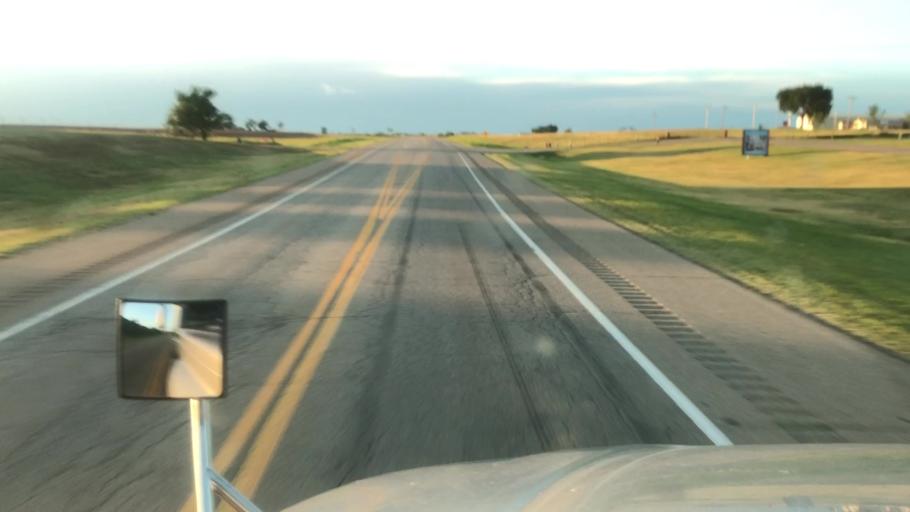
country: US
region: Oklahoma
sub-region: Osage County
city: McCord
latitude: 36.4987
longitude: -97.0738
